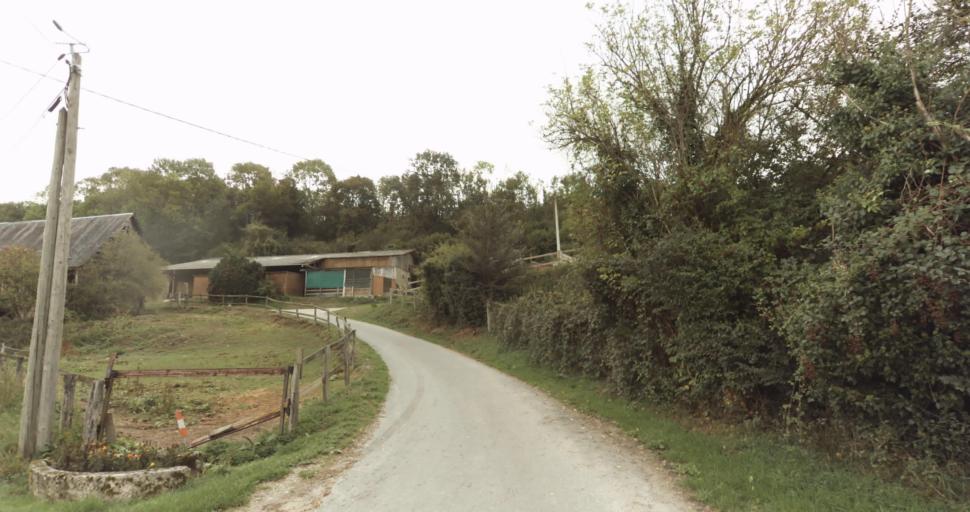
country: FR
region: Lower Normandy
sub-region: Departement de l'Orne
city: Gace
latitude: 48.8238
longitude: 0.2584
